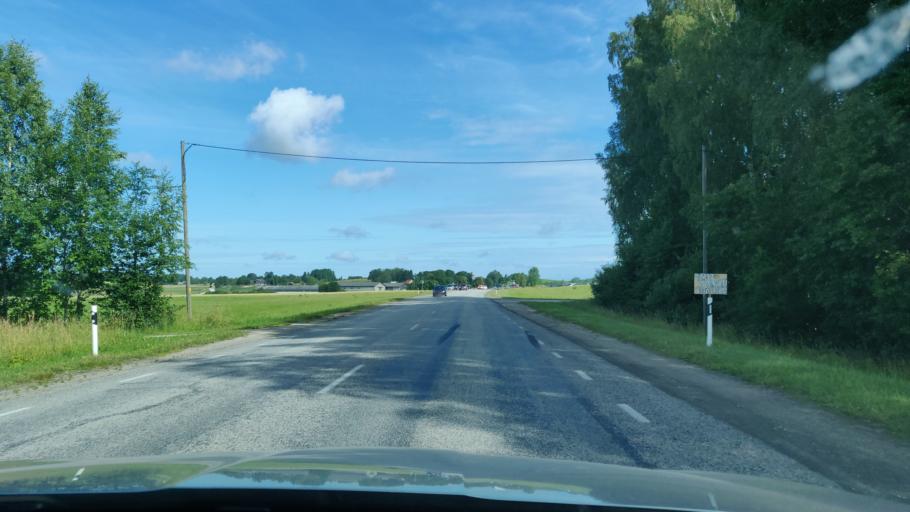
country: EE
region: Tartu
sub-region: Elva linn
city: Elva
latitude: 58.1328
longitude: 26.5223
